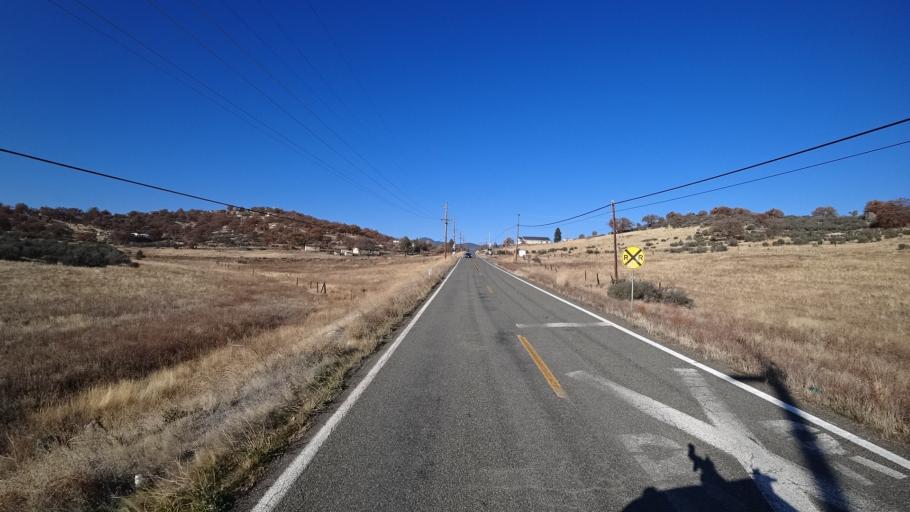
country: US
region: California
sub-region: Siskiyou County
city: Yreka
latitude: 41.7375
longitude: -122.6022
